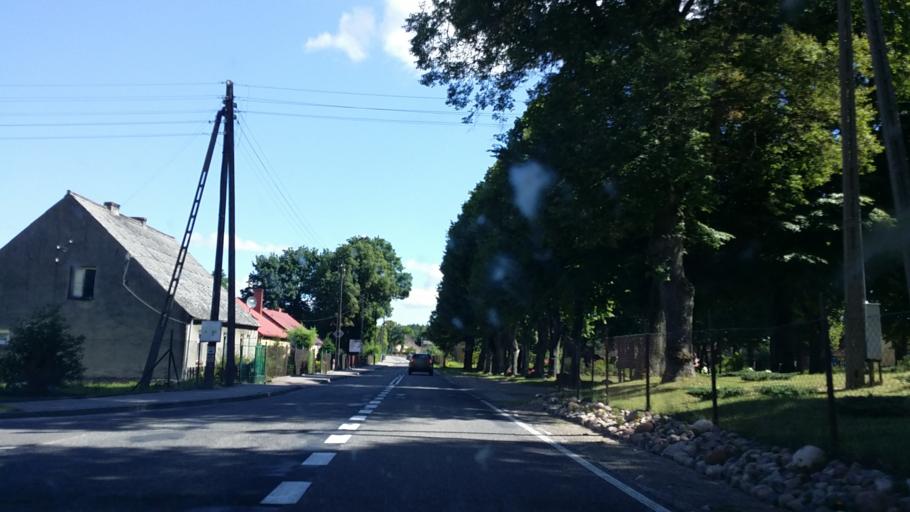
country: PL
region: West Pomeranian Voivodeship
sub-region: Powiat drawski
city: Drawsko Pomorskie
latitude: 53.4413
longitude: 15.8266
